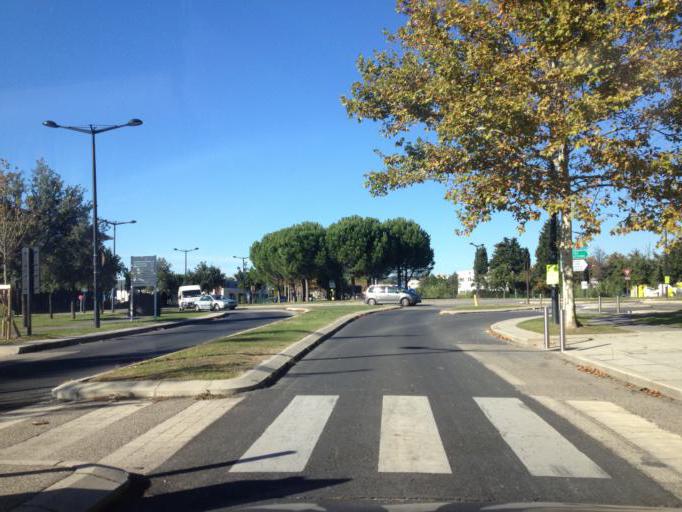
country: FR
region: Provence-Alpes-Cote d'Azur
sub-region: Departement du Vaucluse
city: Avignon
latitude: 43.9273
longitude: 4.7857
